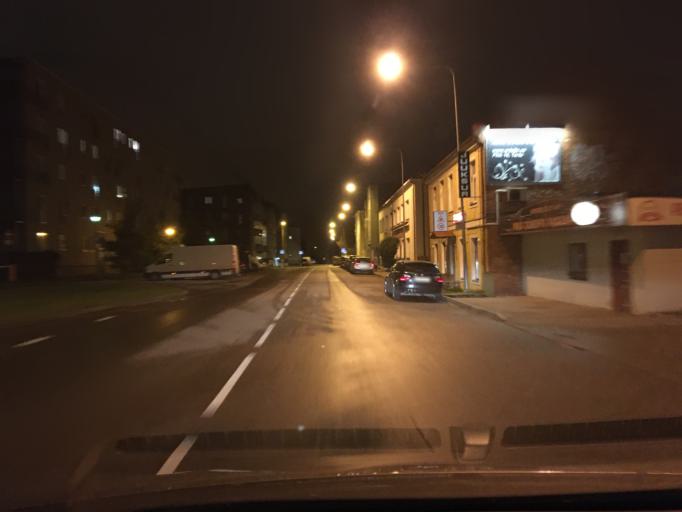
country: EE
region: Tartu
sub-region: Tartu linn
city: Tartu
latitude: 58.3832
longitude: 26.7334
